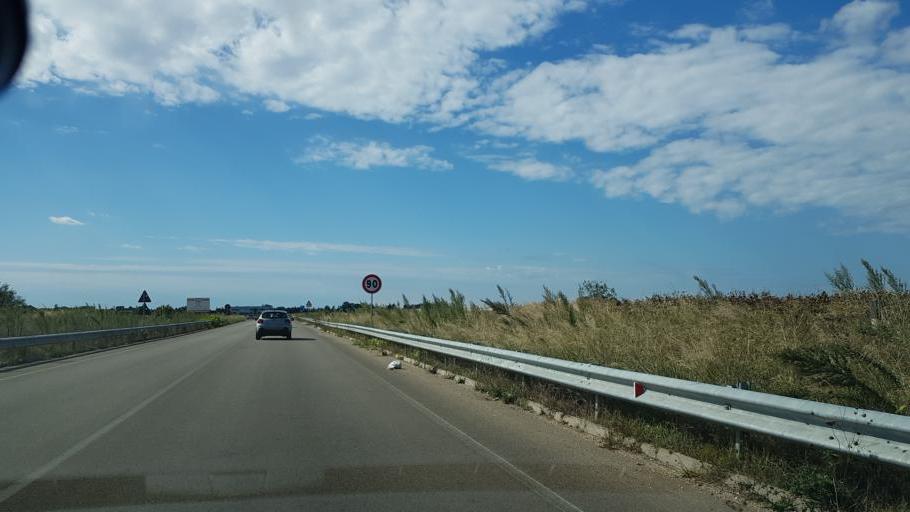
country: IT
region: Apulia
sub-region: Provincia di Lecce
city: Leverano
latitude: 40.2975
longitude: 17.9744
